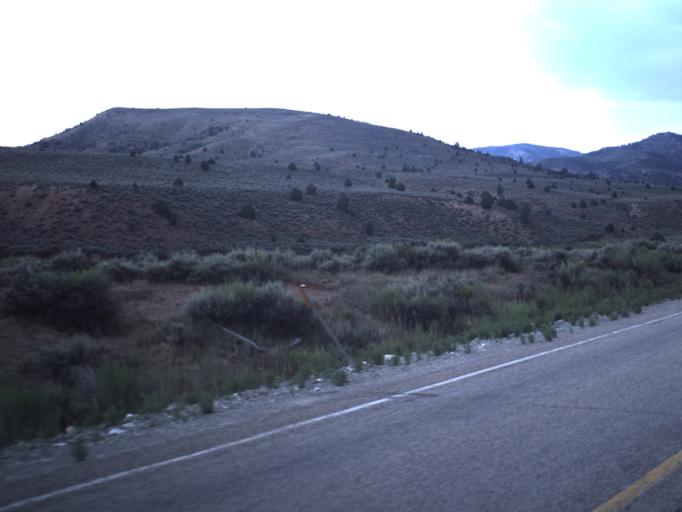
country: US
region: Utah
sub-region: Carbon County
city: Helper
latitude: 39.8189
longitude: -110.7824
